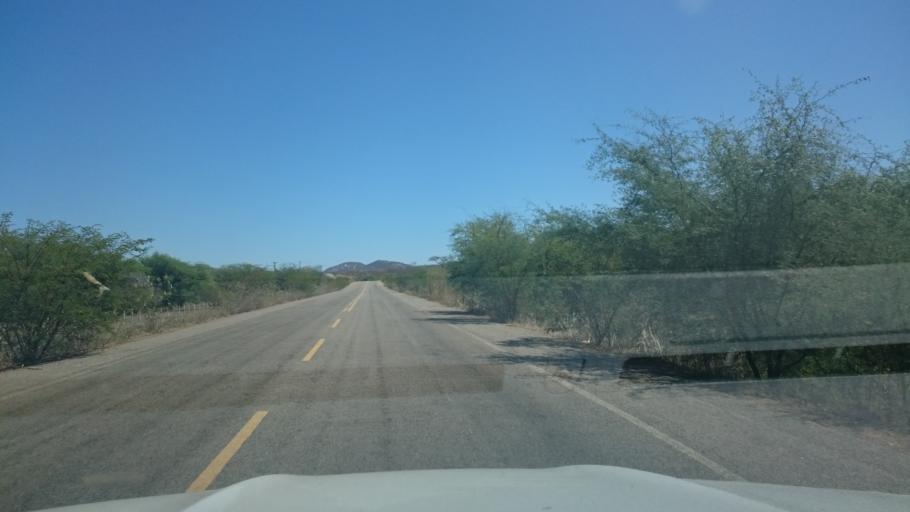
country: BR
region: Rio Grande do Norte
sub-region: Alexandria
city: Alexandria
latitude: -6.1980
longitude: -37.9620
